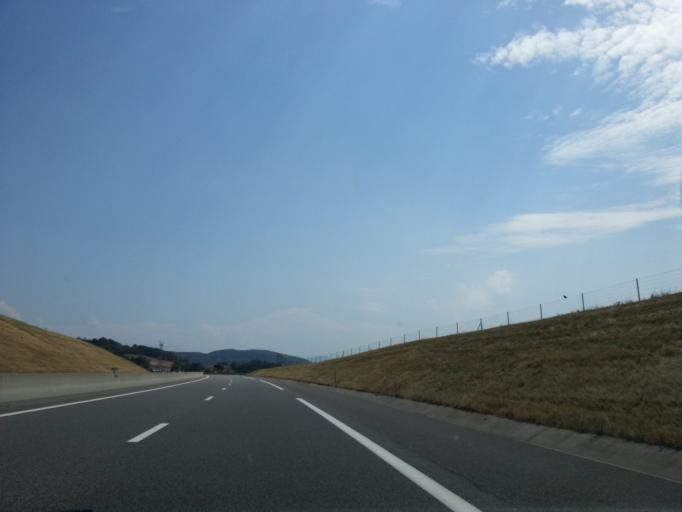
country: FR
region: Rhone-Alpes
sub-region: Departement de la Haute-Savoie
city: Cruseilles
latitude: 46.0469
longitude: 6.0817
